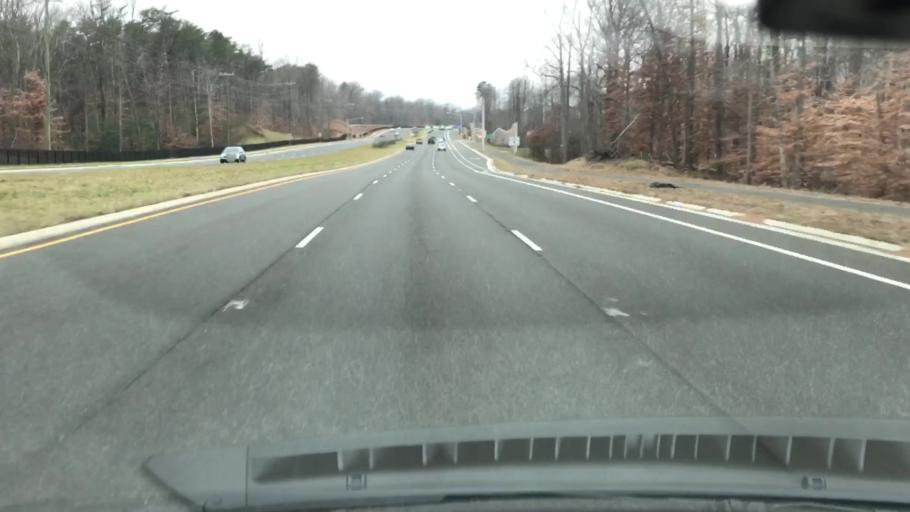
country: US
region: Virginia
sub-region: Fairfax County
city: Newington
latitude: 38.7076
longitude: -77.1788
